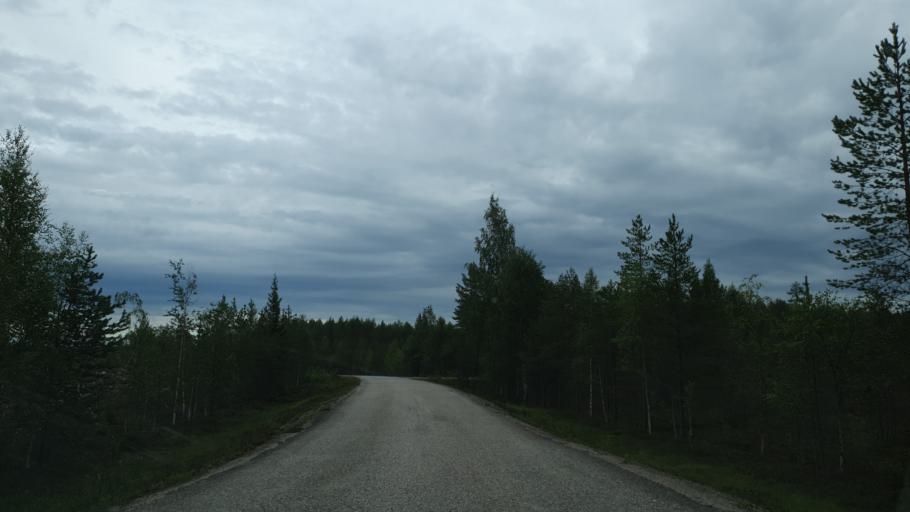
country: FI
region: Kainuu
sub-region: Kehys-Kainuu
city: Kuhmo
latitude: 64.3515
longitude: 29.1621
